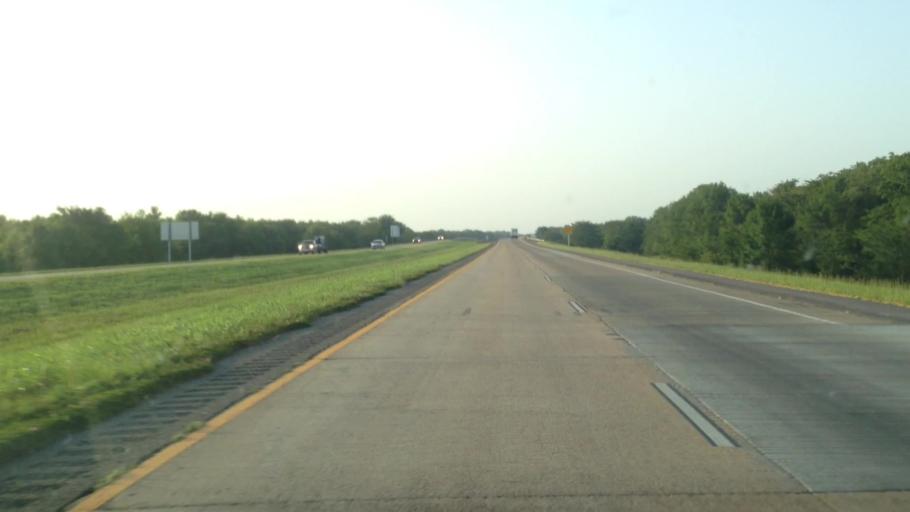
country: US
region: Louisiana
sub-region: Natchitoches Parish
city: Vienna Bend
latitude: 31.6006
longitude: -93.0417
